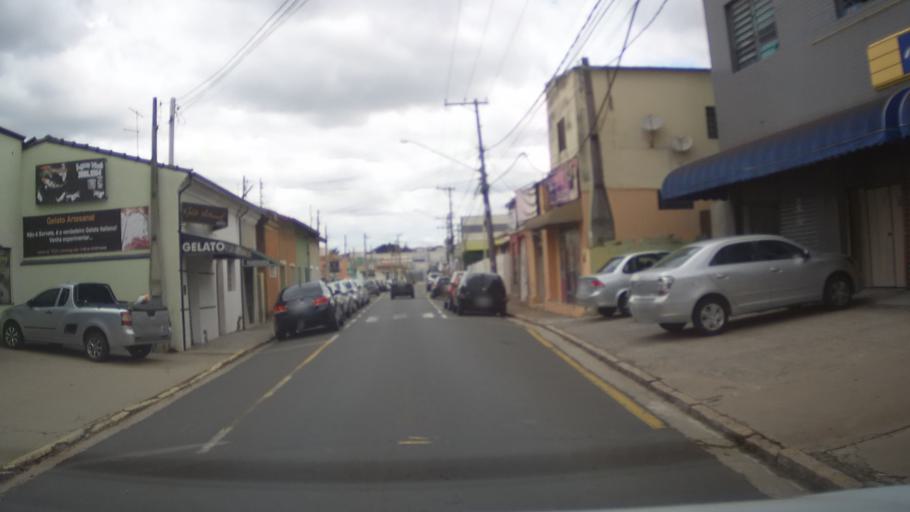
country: BR
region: Sao Paulo
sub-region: Vinhedo
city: Vinhedo
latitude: -23.0283
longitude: -46.9789
